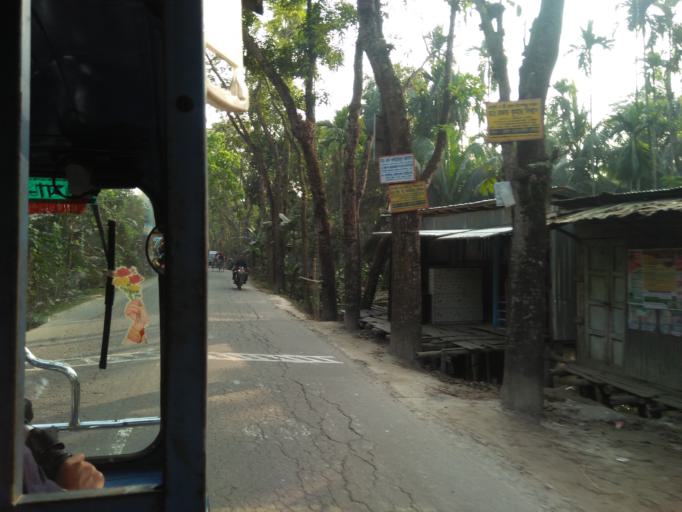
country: BD
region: Barisal
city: Bhola
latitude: 22.7069
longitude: 90.6401
